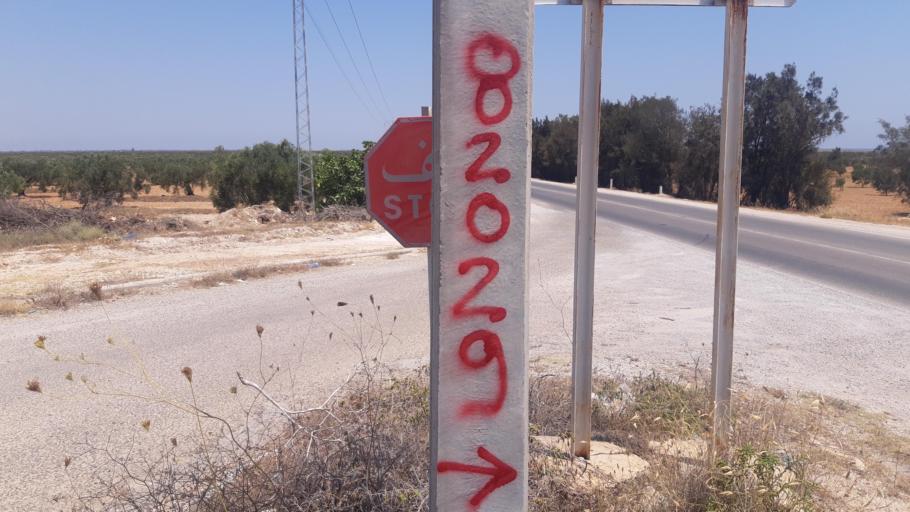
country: TN
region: Al Mahdiyah
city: Mellouleche
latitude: 35.1762
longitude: 11.0670
